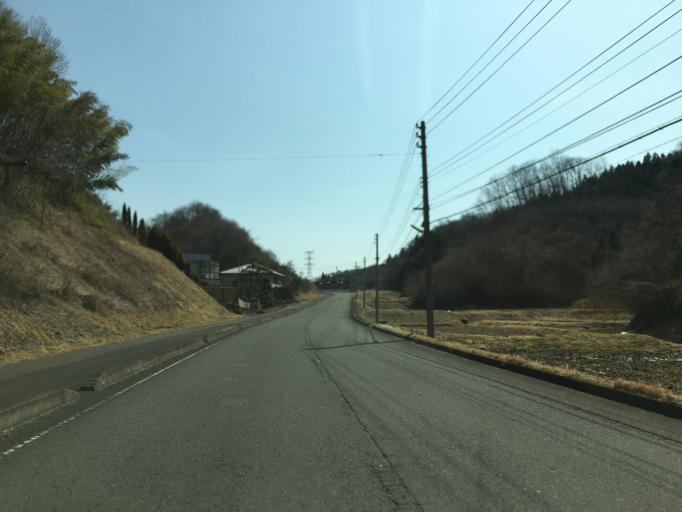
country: JP
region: Fukushima
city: Ishikawa
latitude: 37.0418
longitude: 140.4710
